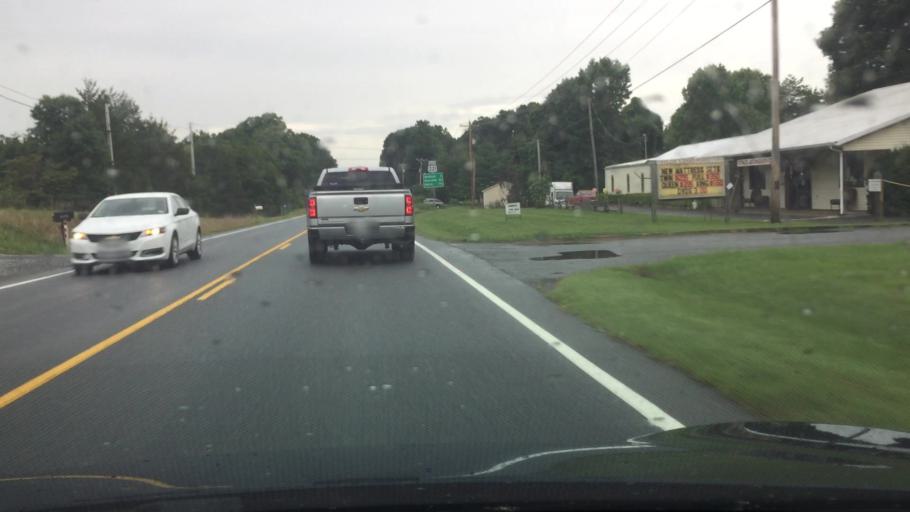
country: US
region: Virginia
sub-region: City of Bedford
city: Bedford
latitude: 37.3635
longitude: -79.4434
